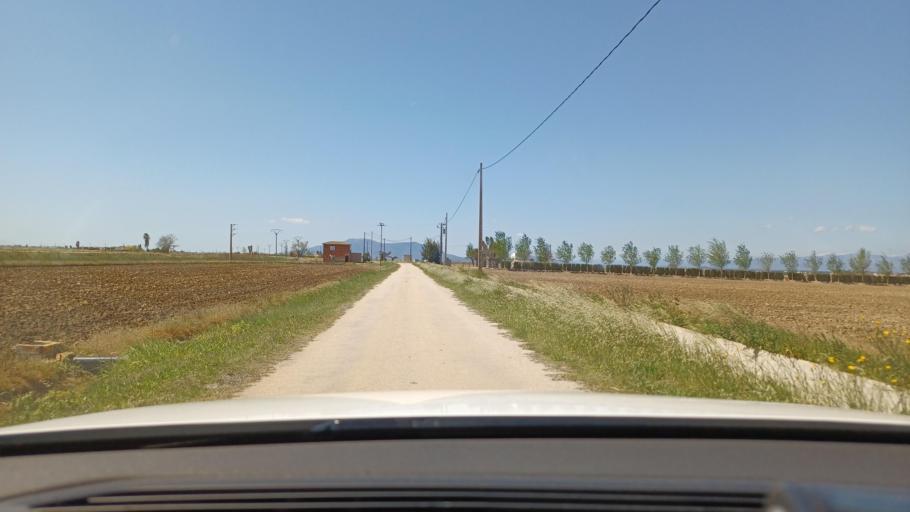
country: ES
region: Catalonia
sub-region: Provincia de Tarragona
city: L'Ampolla
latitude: 40.7772
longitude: 0.7139
